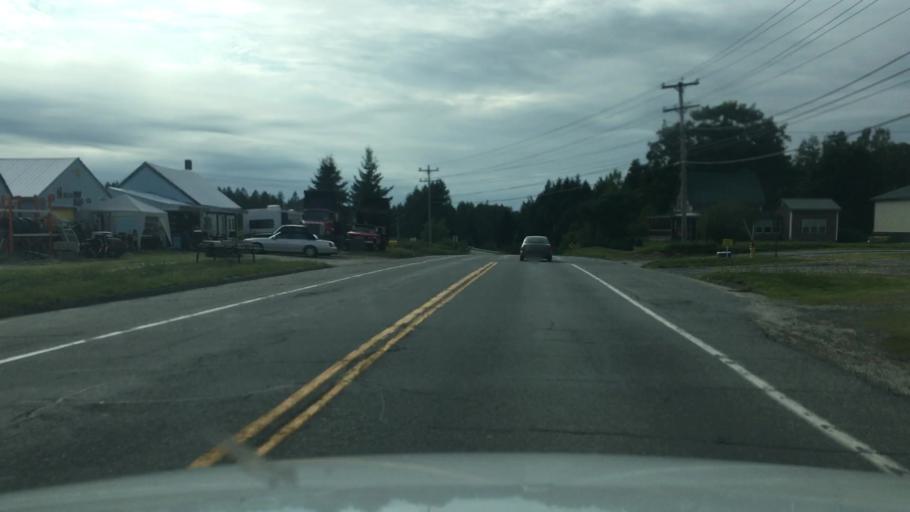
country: US
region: Maine
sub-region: Washington County
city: Addison
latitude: 44.6220
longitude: -67.8184
